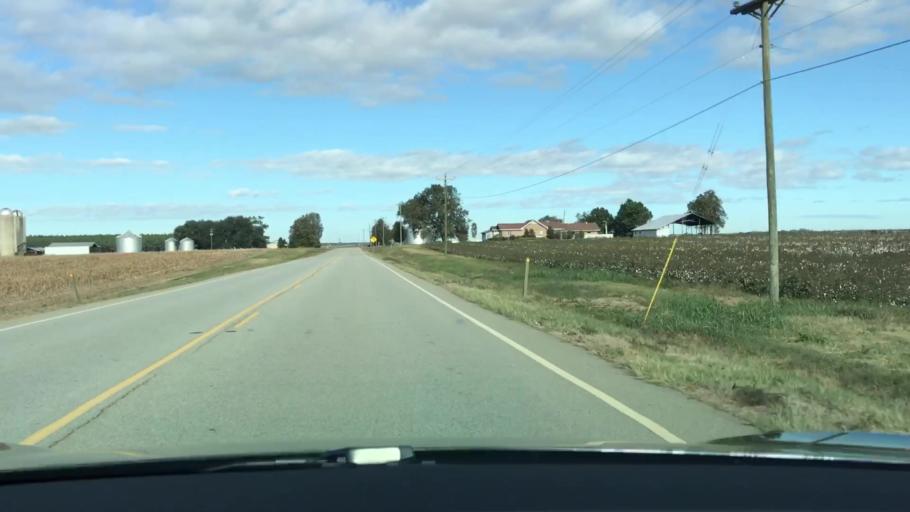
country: US
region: Georgia
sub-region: Jefferson County
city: Louisville
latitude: 33.1049
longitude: -82.4248
